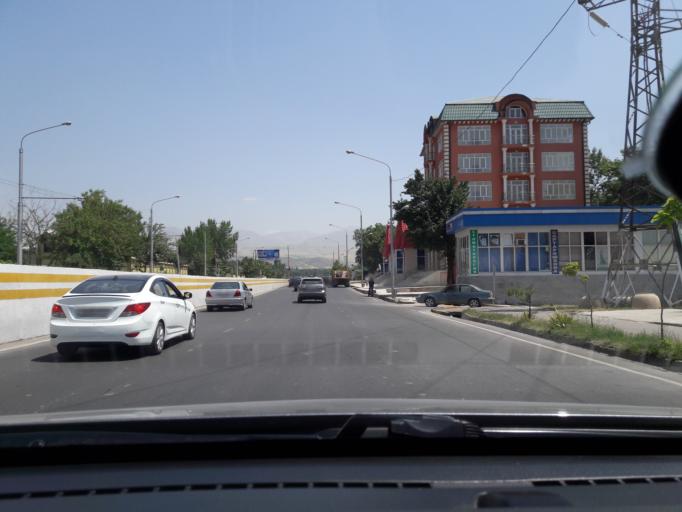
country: TJ
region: Dushanbe
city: Dushanbe
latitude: 38.5938
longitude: 68.7530
